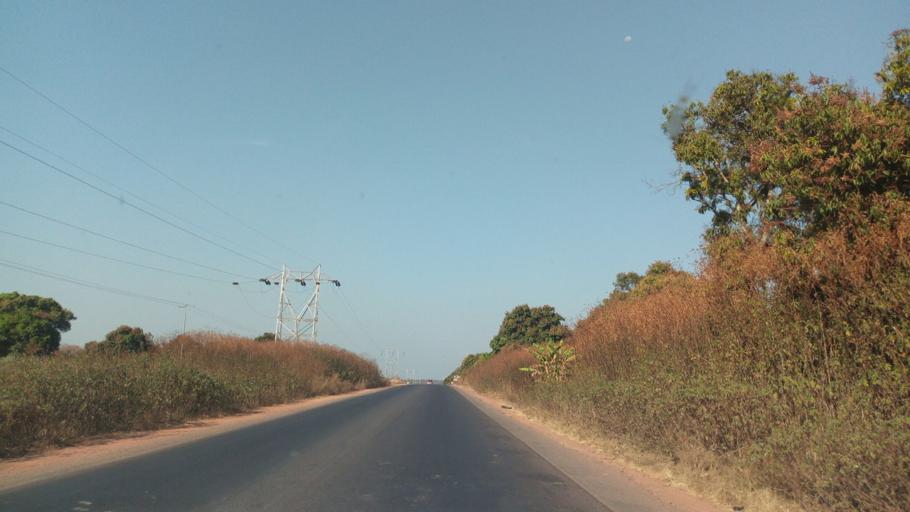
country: CD
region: Katanga
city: Likasi
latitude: -11.0011
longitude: 26.8750
